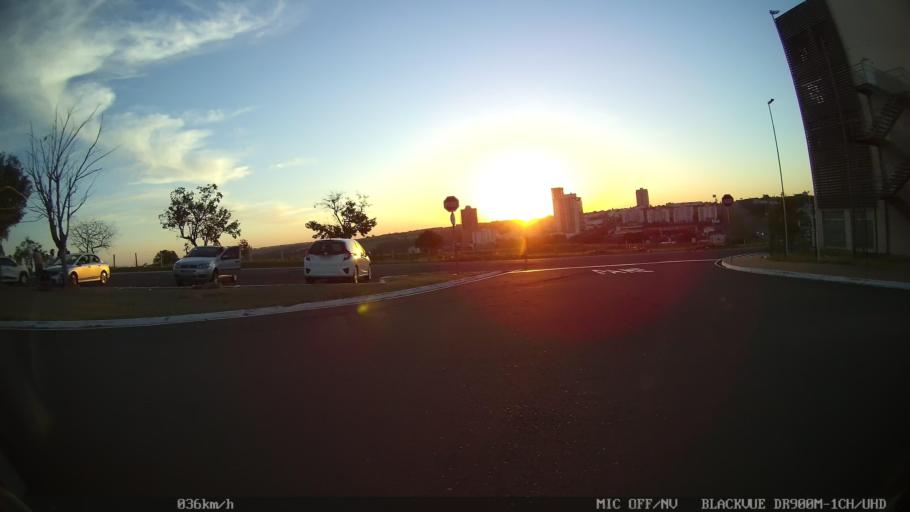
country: BR
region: Sao Paulo
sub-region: Franca
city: Franca
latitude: -20.5568
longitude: -47.4080
